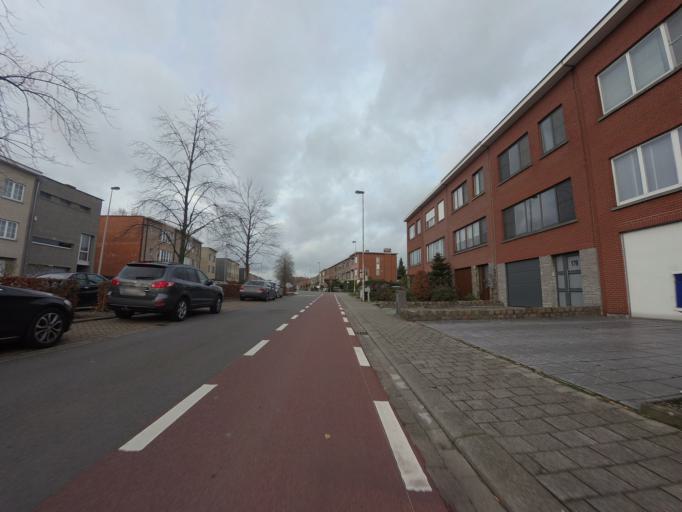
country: BE
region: Flanders
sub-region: Provincie Antwerpen
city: Hemiksem
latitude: 51.1377
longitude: 4.3460
